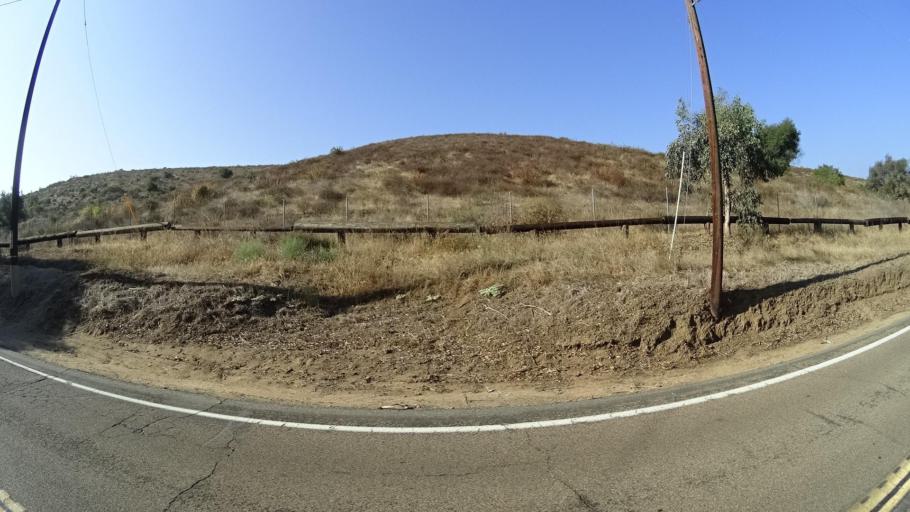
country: US
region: California
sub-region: San Diego County
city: Bonsall
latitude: 33.2897
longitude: -117.2309
